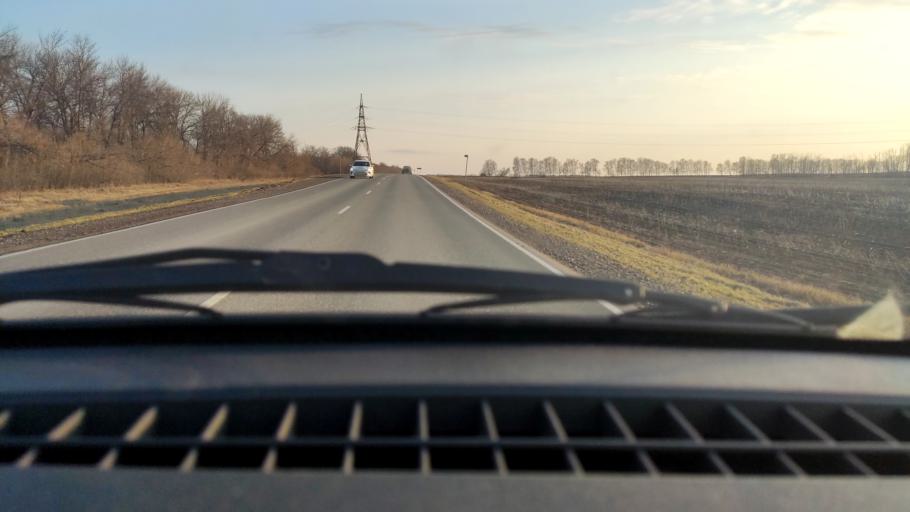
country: RU
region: Bashkortostan
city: Chishmy
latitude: 54.4841
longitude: 55.2711
